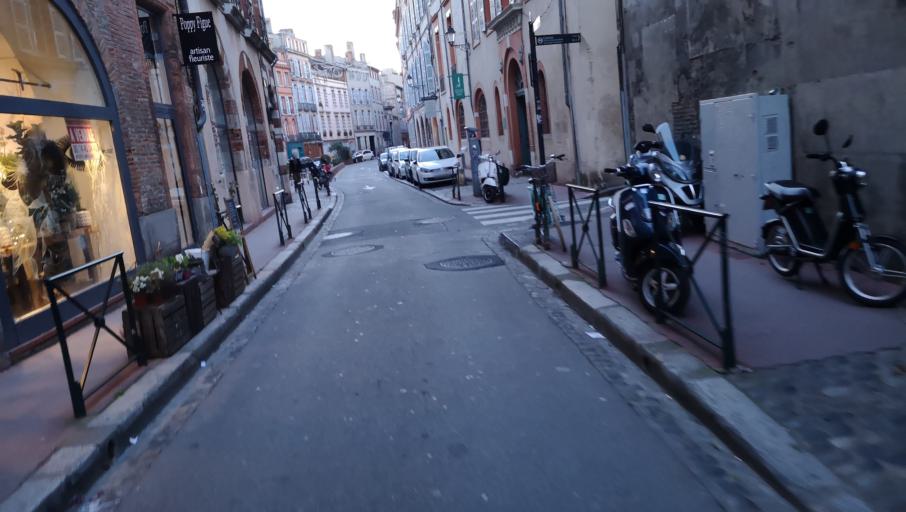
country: FR
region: Midi-Pyrenees
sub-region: Departement de la Haute-Garonne
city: Toulouse
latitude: 43.5990
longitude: 1.4491
